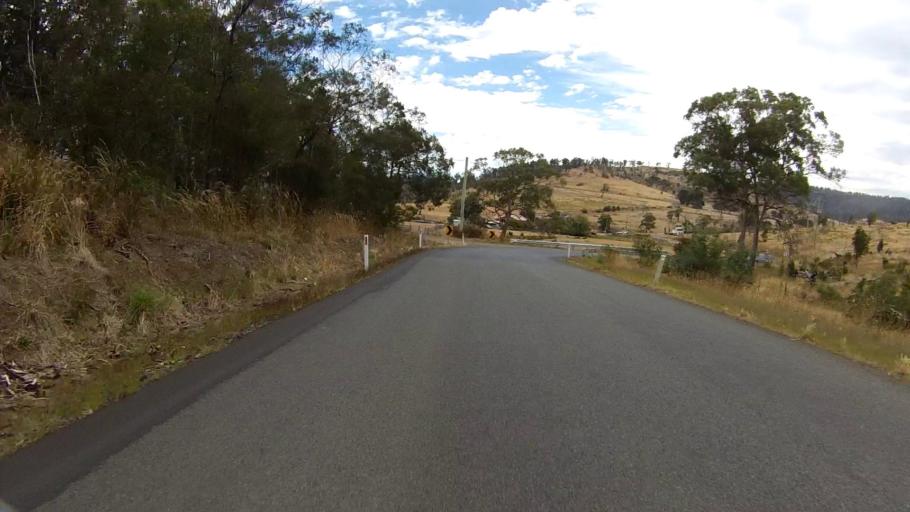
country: AU
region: Tasmania
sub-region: Sorell
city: Sorell
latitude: -42.8741
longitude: 147.7029
